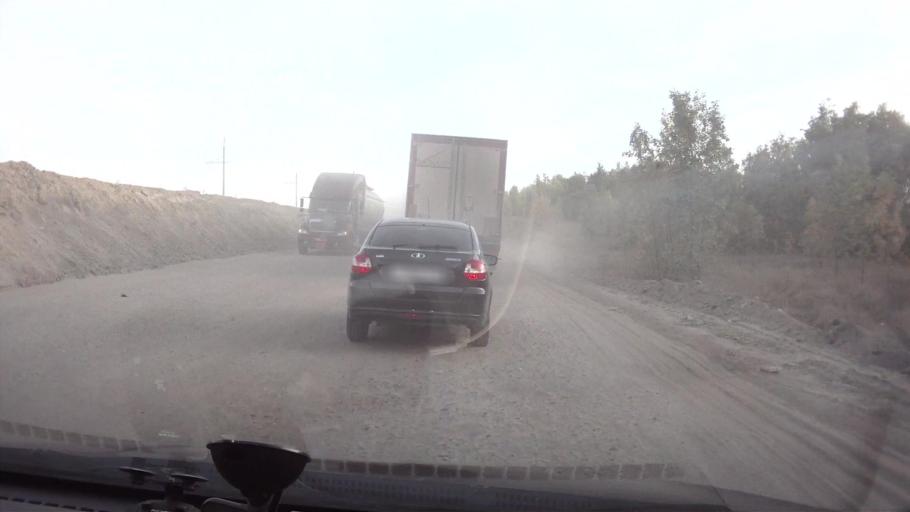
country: RU
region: Saratov
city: Krasnoarmeysk
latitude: 51.2216
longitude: 45.6466
